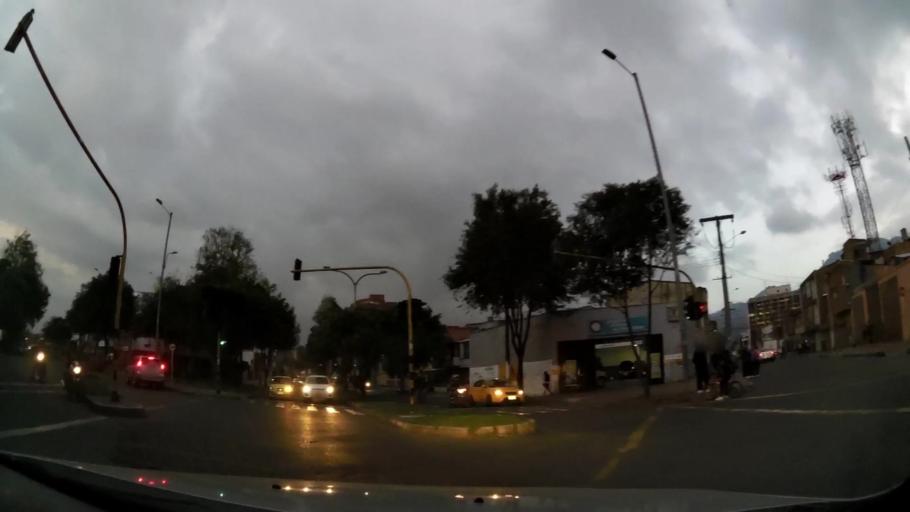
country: CO
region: Bogota D.C.
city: Bogota
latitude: 4.6219
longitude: -74.0807
